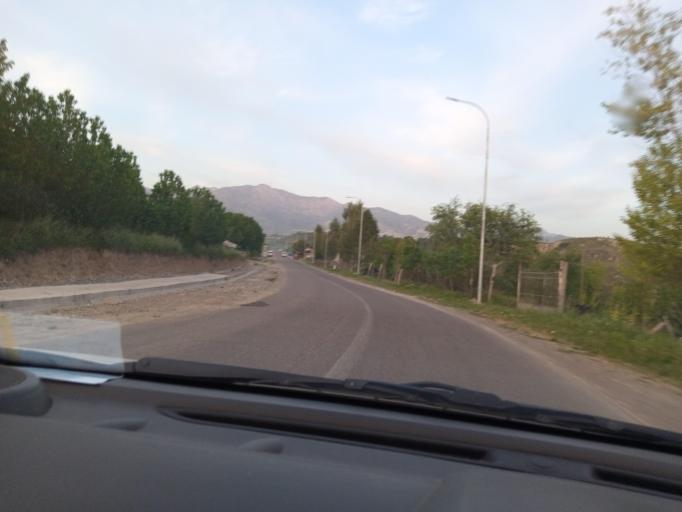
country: UZ
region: Toshkent
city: Parkent
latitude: 41.2452
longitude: 69.7425
